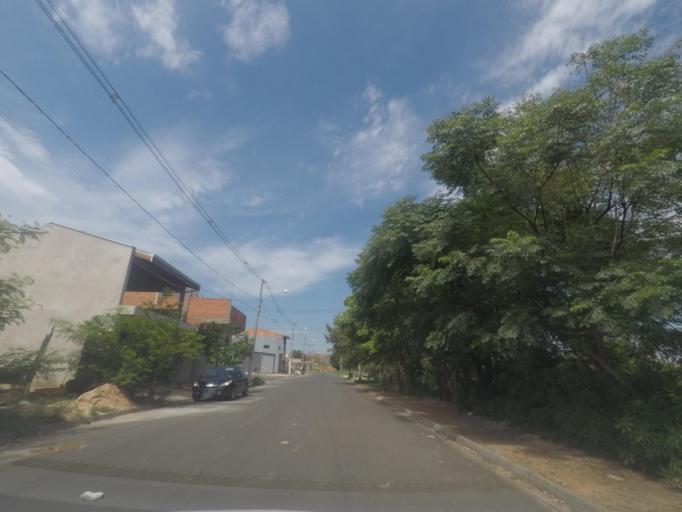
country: BR
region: Sao Paulo
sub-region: Sumare
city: Sumare
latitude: -22.7995
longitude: -47.2620
